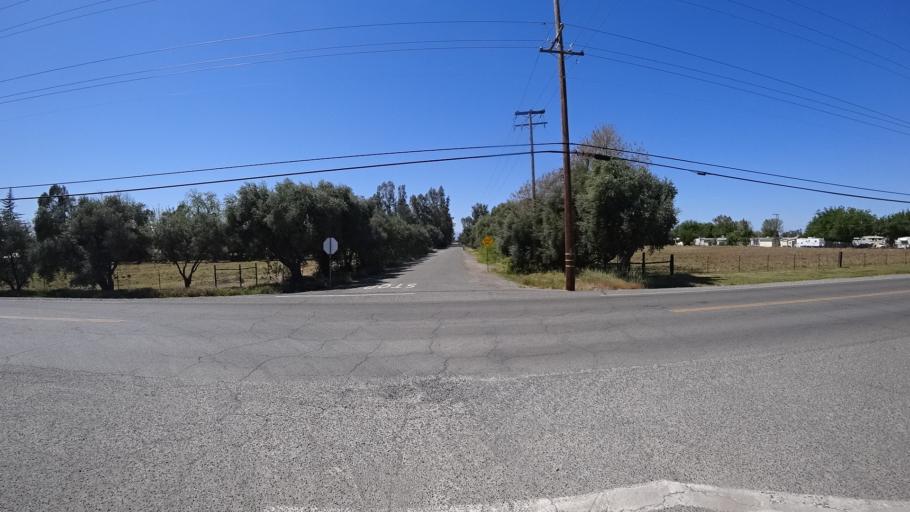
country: US
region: California
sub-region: Glenn County
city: Orland
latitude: 39.7329
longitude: -122.1967
